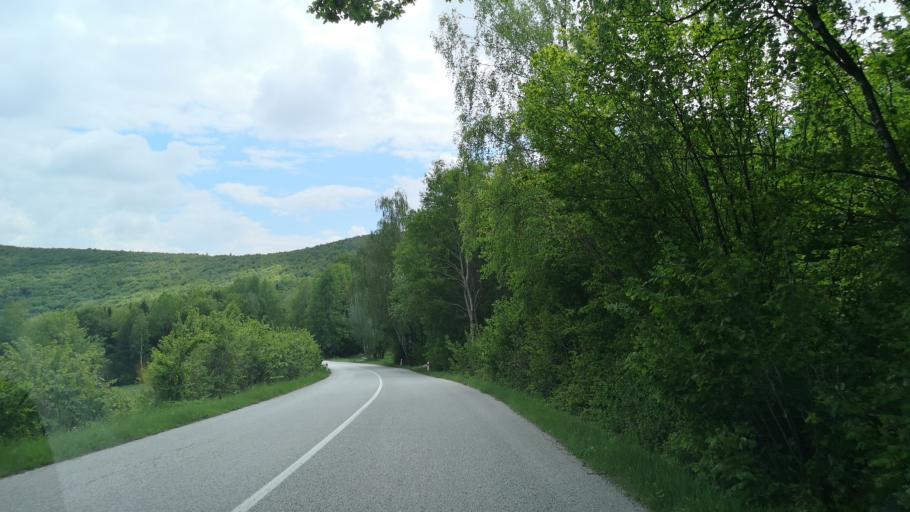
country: SK
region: Banskobystricky
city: Revuca
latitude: 48.6463
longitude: 20.2990
